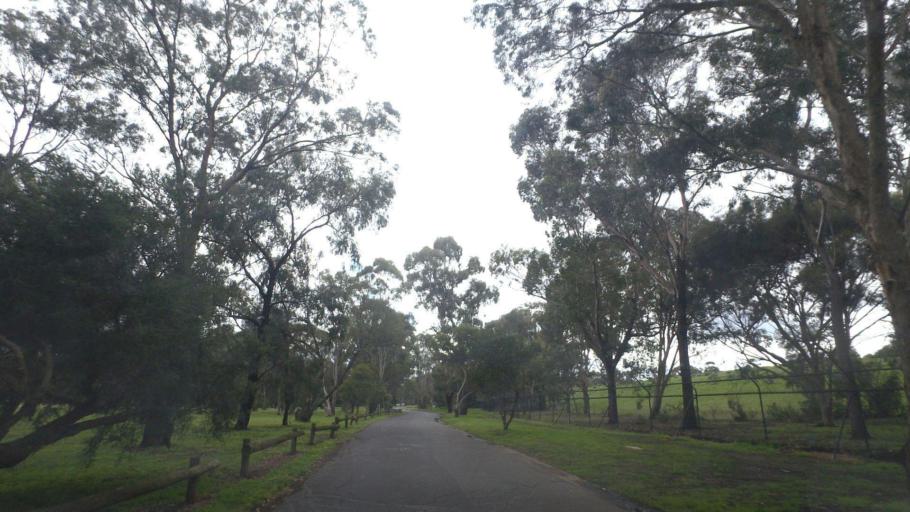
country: AU
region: Victoria
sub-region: Darebin
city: Kingsbury
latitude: -37.7081
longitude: 145.0411
